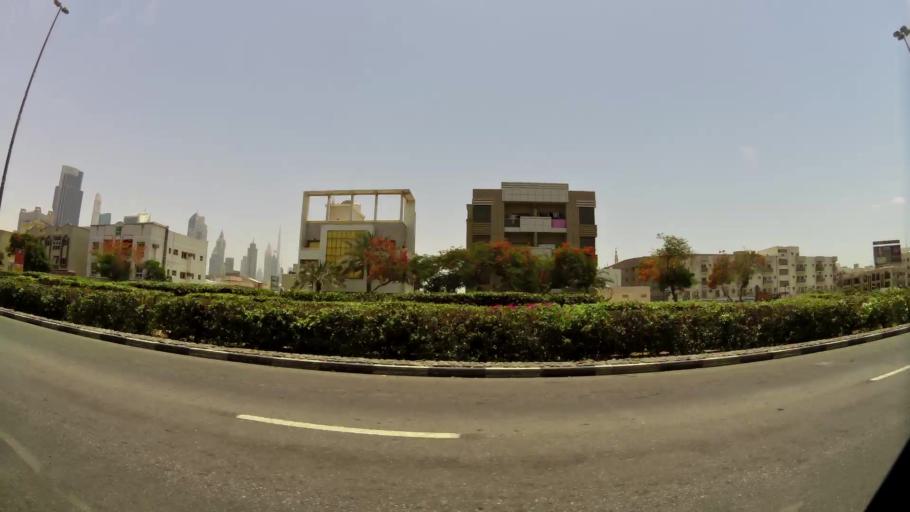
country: AE
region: Ash Shariqah
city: Sharjah
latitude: 25.2345
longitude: 55.2799
